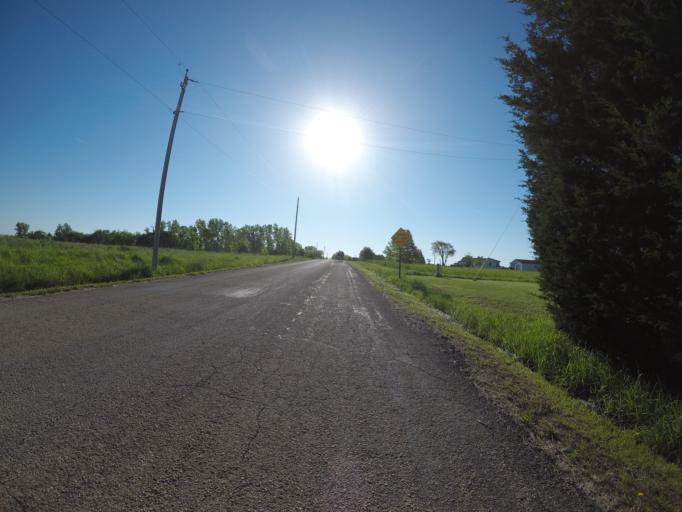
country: US
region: Kansas
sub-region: Shawnee County
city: Topeka
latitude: 39.0369
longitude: -95.5610
